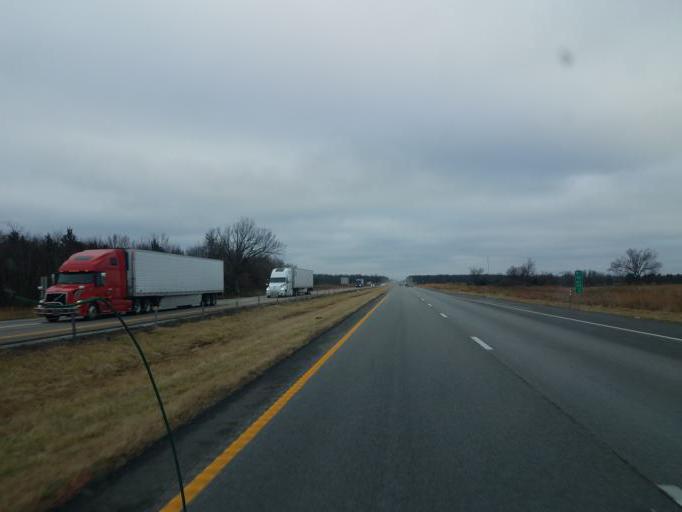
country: US
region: Missouri
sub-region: Webster County
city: Marshfield
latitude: 37.5005
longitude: -92.8436
